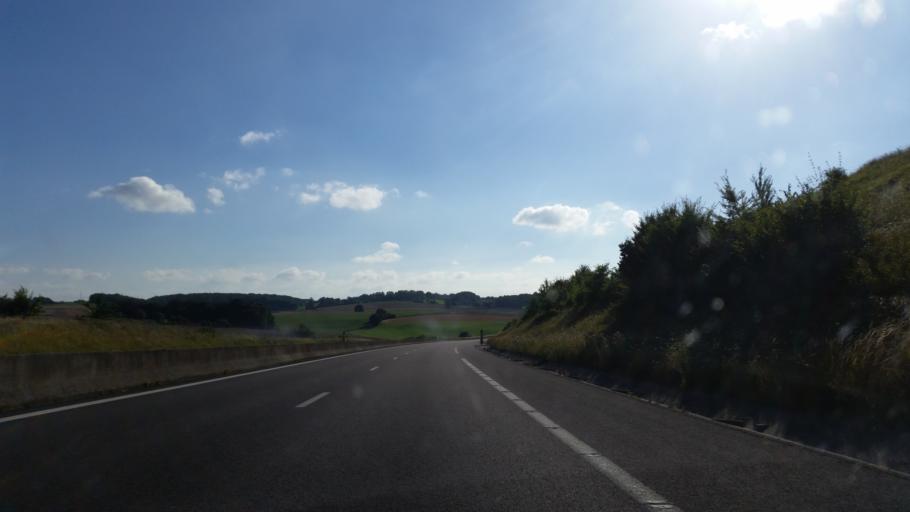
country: FR
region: Haute-Normandie
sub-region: Departement de la Seine-Maritime
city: Gaillefontaine
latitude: 49.7374
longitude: 1.5730
